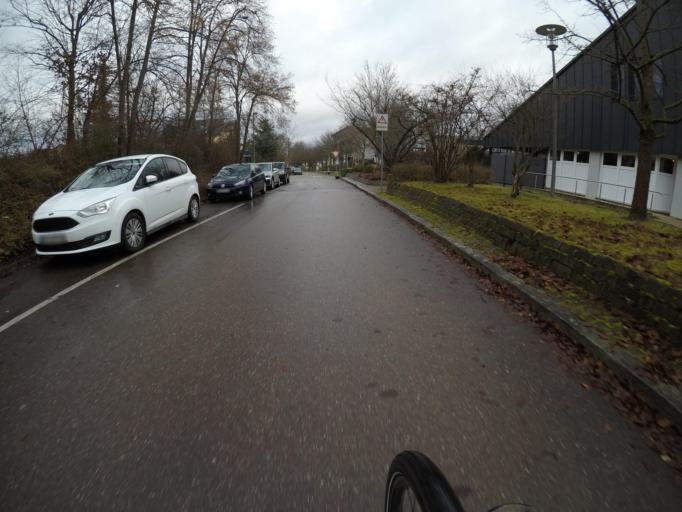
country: DE
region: Baden-Wuerttemberg
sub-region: Regierungsbezirk Stuttgart
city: Gerlingen
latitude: 48.8001
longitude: 9.0766
